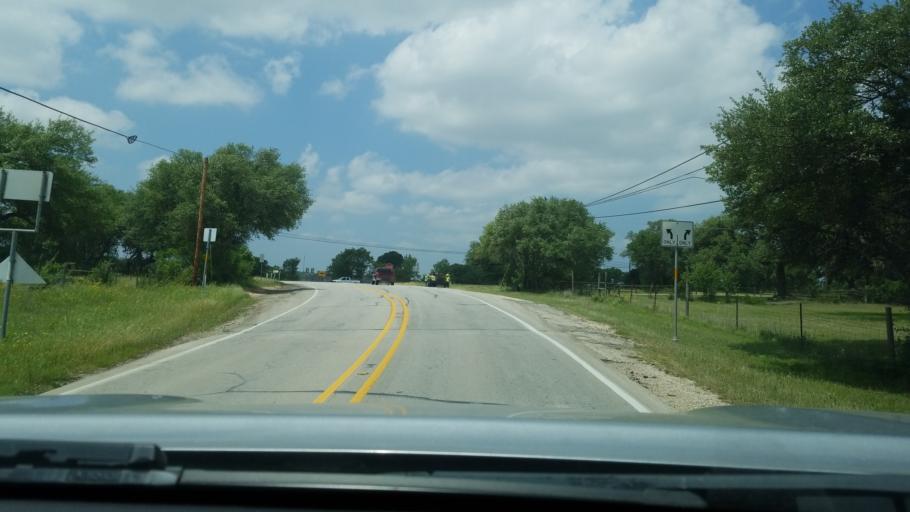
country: US
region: Texas
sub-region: Hays County
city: Dripping Springs
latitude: 30.1673
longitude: -98.0858
